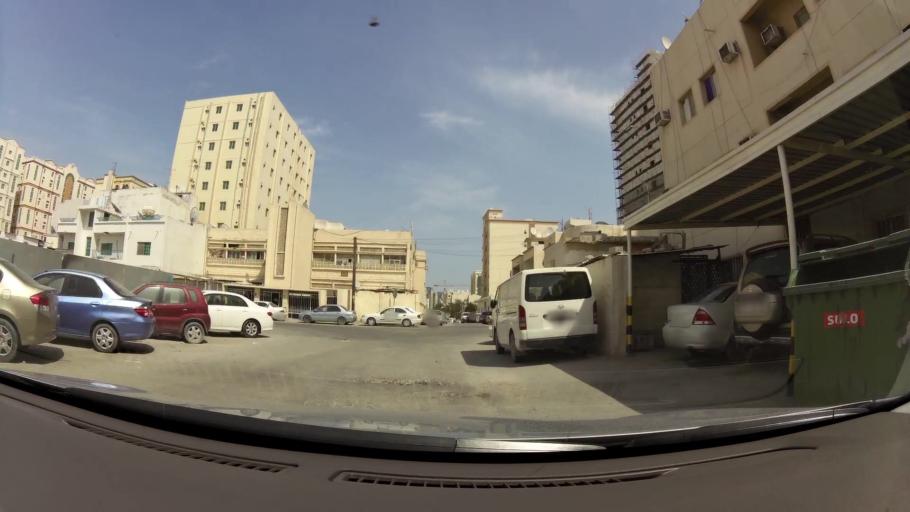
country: QA
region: Baladiyat ad Dawhah
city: Doha
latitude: 25.2770
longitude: 51.5306
